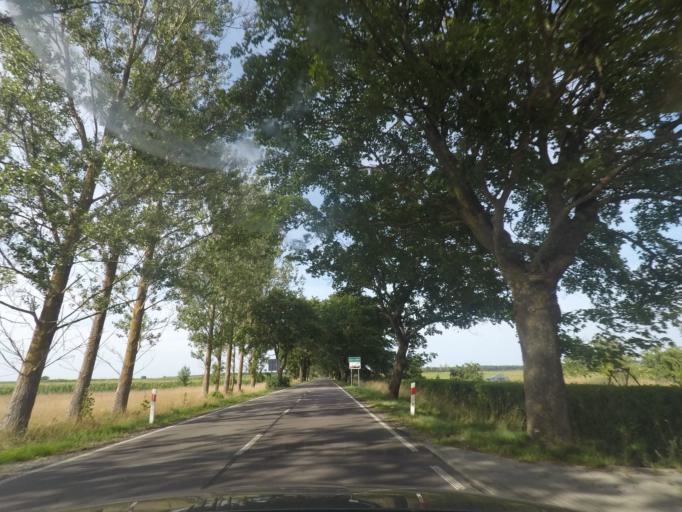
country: PL
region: Pomeranian Voivodeship
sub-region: Powiat leborski
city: Leba
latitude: 54.6465
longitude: 17.5527
